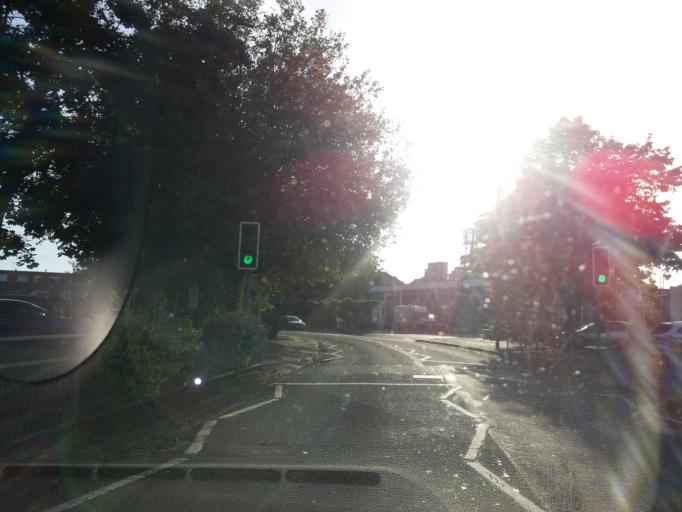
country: GB
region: England
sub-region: Surrey
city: Chertsey
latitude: 51.3907
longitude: -0.5027
